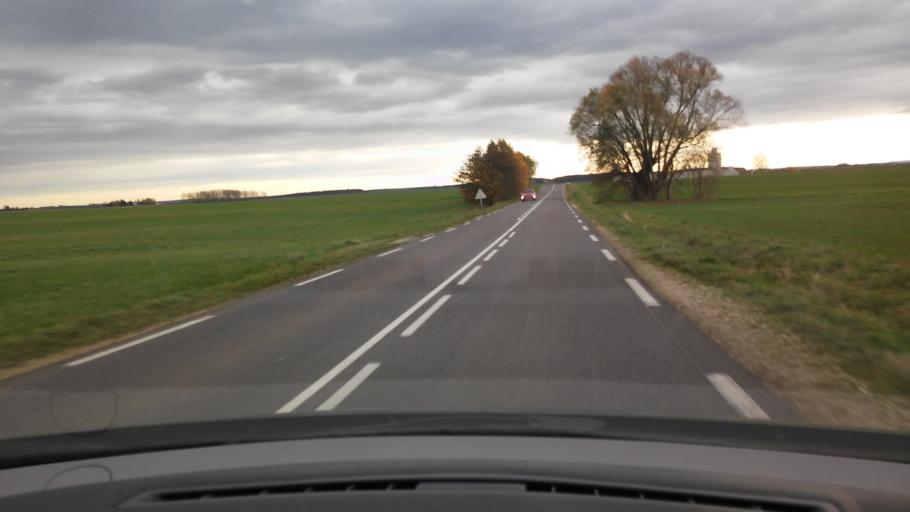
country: FR
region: Lorraine
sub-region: Departement de la Moselle
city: Retonfey
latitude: 49.1512
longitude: 6.3091
